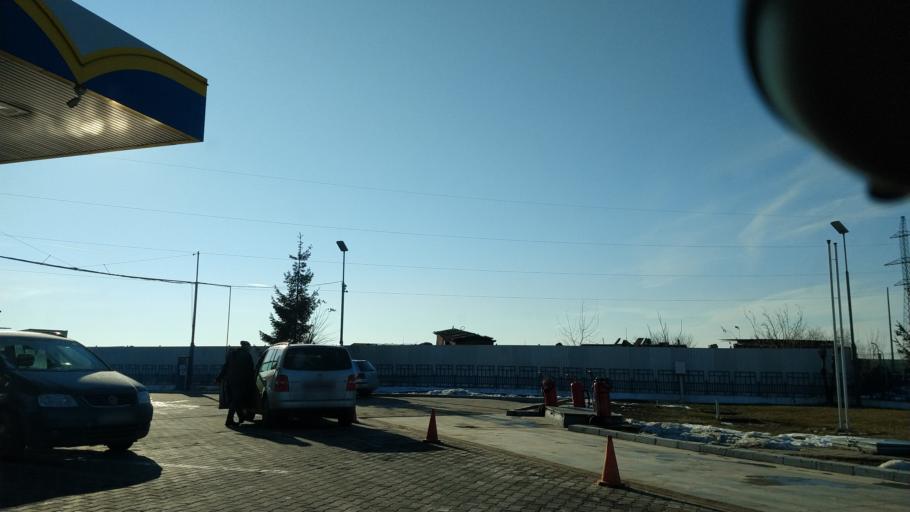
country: RO
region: Neamt
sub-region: Municipiul Roman
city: Roman
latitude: 46.9249
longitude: 26.9092
